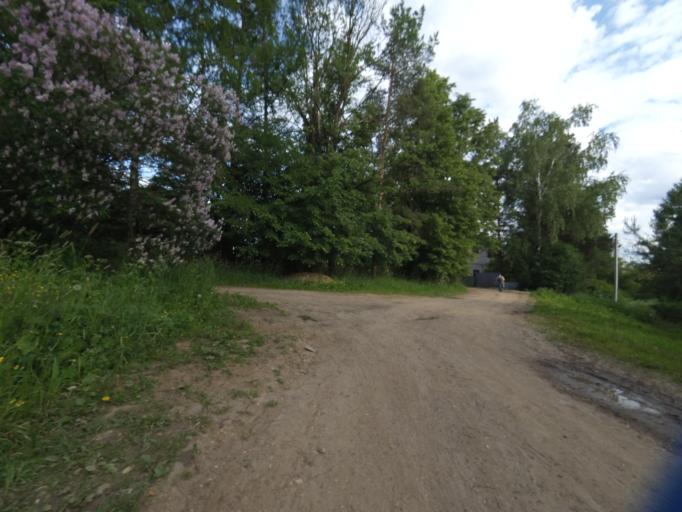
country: RU
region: Moskovskaya
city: Nekrasovskiy
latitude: 56.0727
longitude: 37.4969
